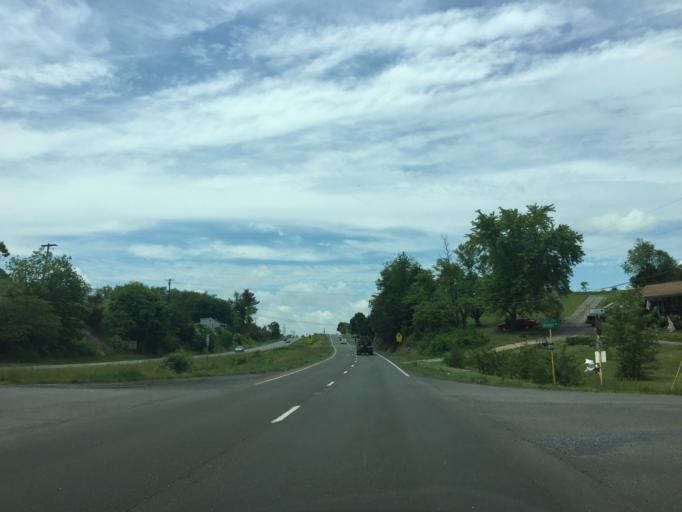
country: US
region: Virginia
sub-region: City of Winchester
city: Winchester
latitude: 39.2687
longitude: -78.2414
